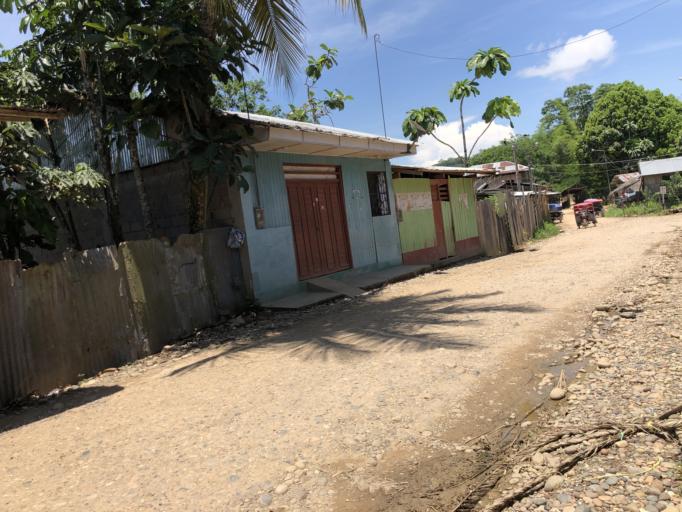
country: PE
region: Loreto
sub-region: Datem Del Maranon
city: Saramiriza
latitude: -4.6008
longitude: -77.8682
